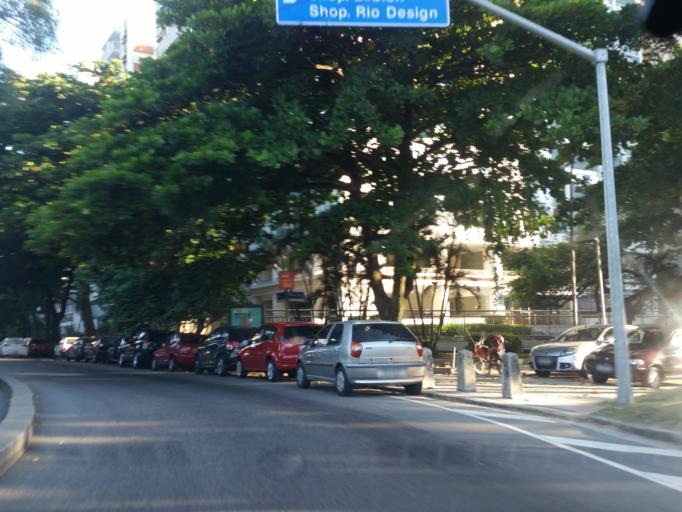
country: BR
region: Rio de Janeiro
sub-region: Rio De Janeiro
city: Rio de Janeiro
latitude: -22.9790
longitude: -43.2184
